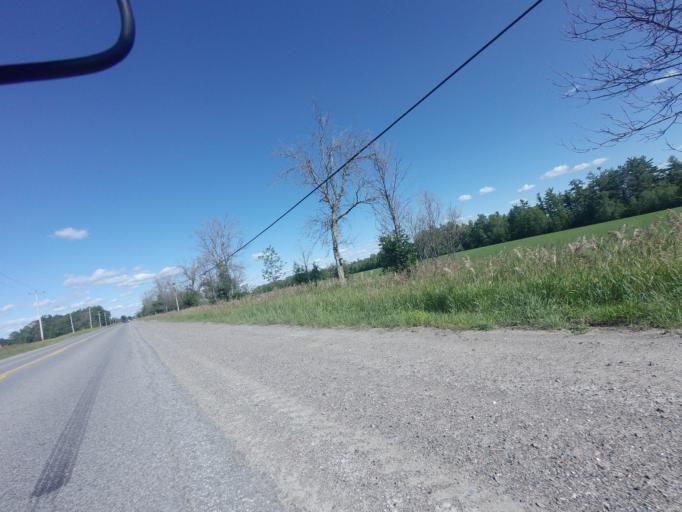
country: CA
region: Ontario
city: Arnprior
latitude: 45.4112
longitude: -76.4420
